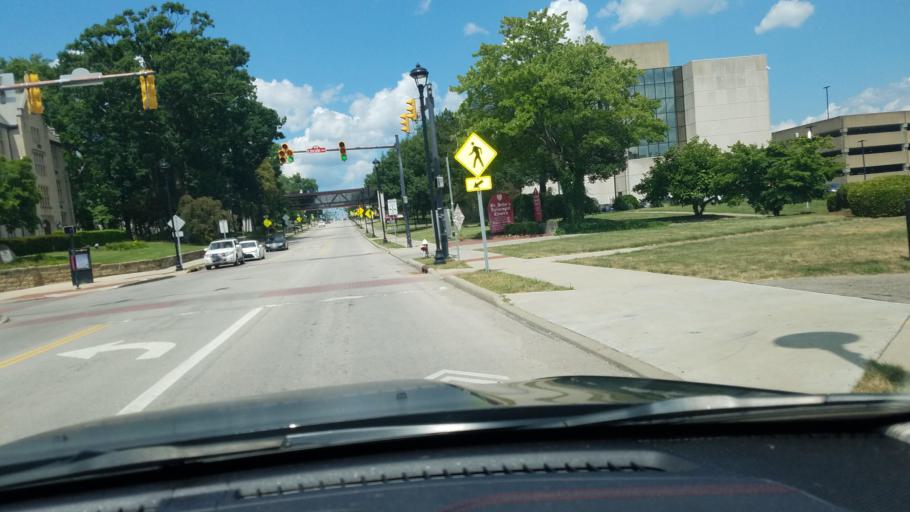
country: US
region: Ohio
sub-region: Mahoning County
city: Youngstown
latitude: 41.1036
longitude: -80.6466
